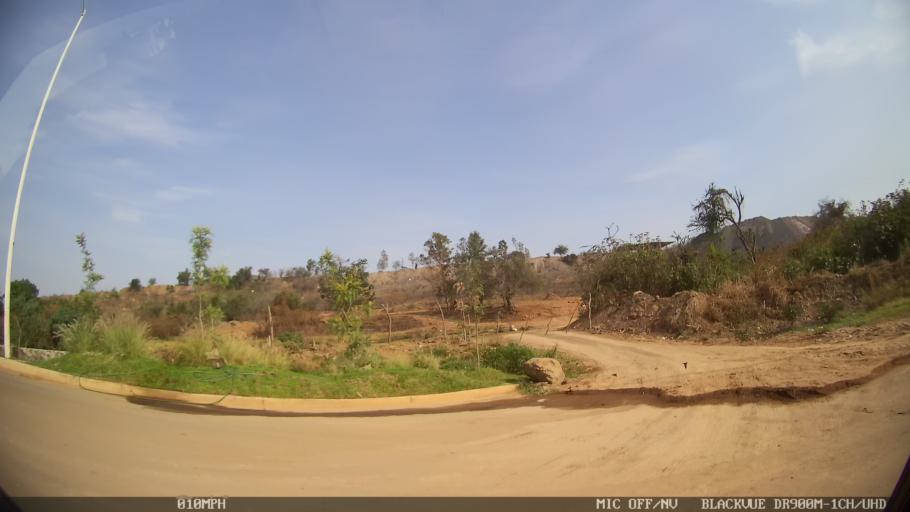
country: MX
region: Jalisco
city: Tonala
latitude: 20.6249
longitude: -103.2193
